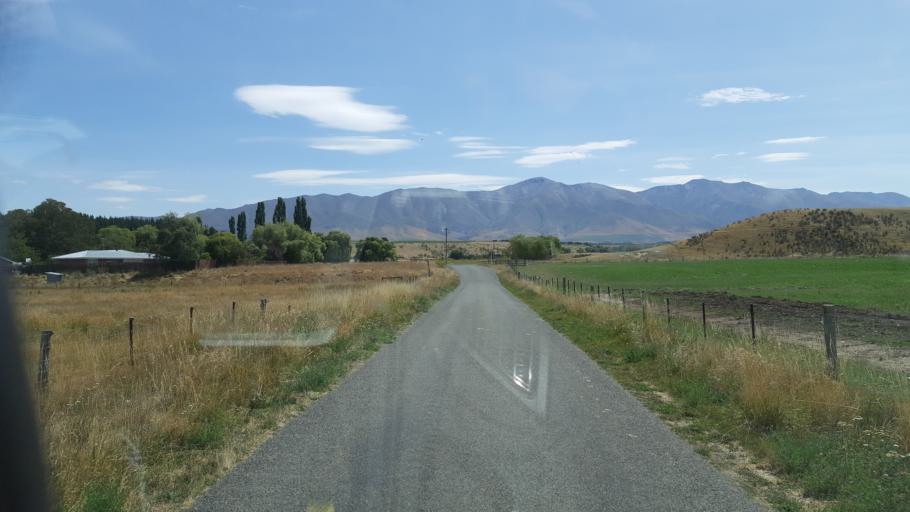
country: NZ
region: Otago
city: Oamaru
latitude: -44.6576
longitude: 170.5964
